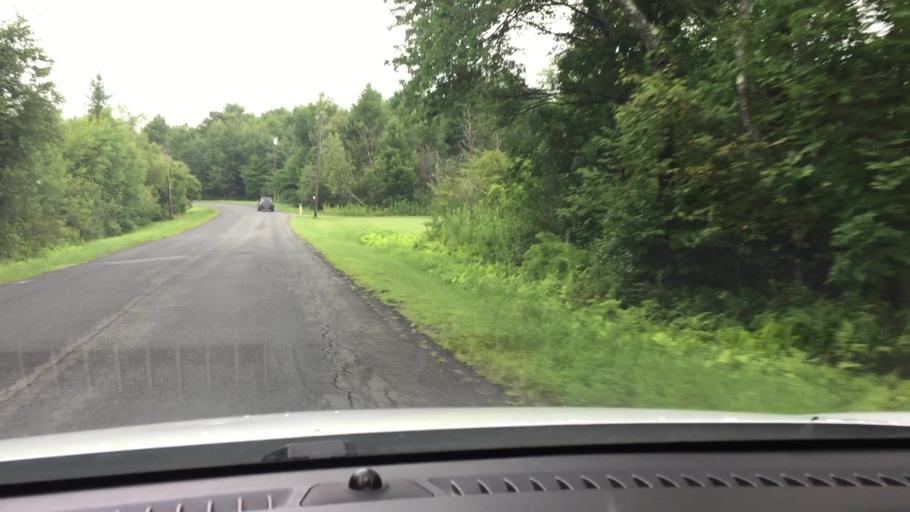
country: US
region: Massachusetts
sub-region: Berkshire County
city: Hinsdale
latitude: 42.4143
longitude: -73.0599
